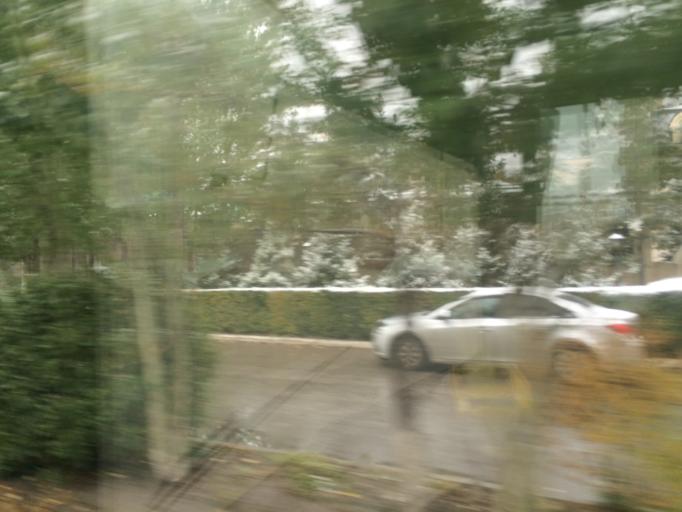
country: KZ
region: Astana Qalasy
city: Astana
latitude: 51.1427
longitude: 71.4450
